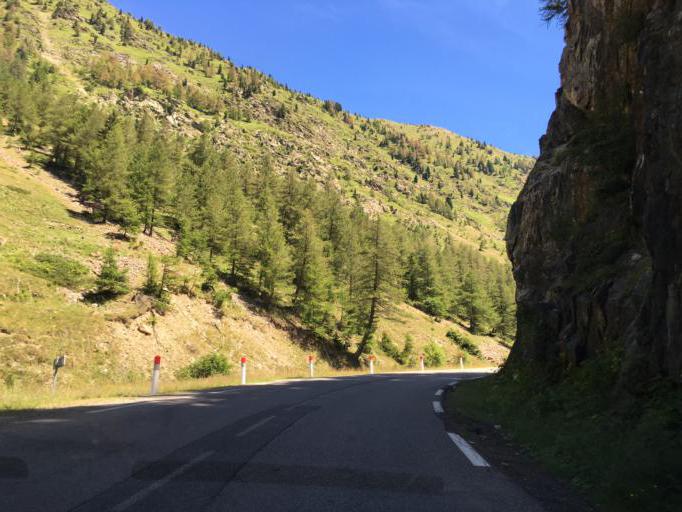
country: IT
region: Piedmont
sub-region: Provincia di Cuneo
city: Vinadio
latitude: 44.2071
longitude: 7.1123
